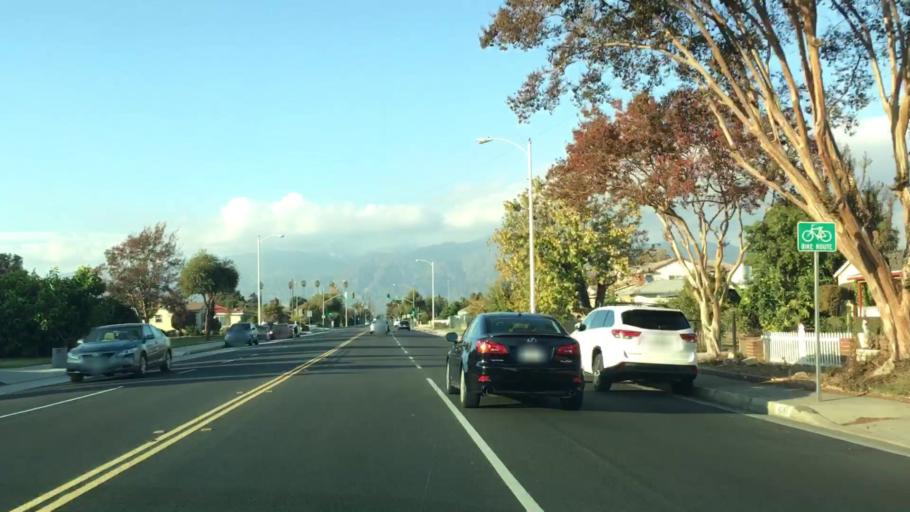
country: US
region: California
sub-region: Los Angeles County
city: Temple City
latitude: 34.0920
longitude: -118.0578
